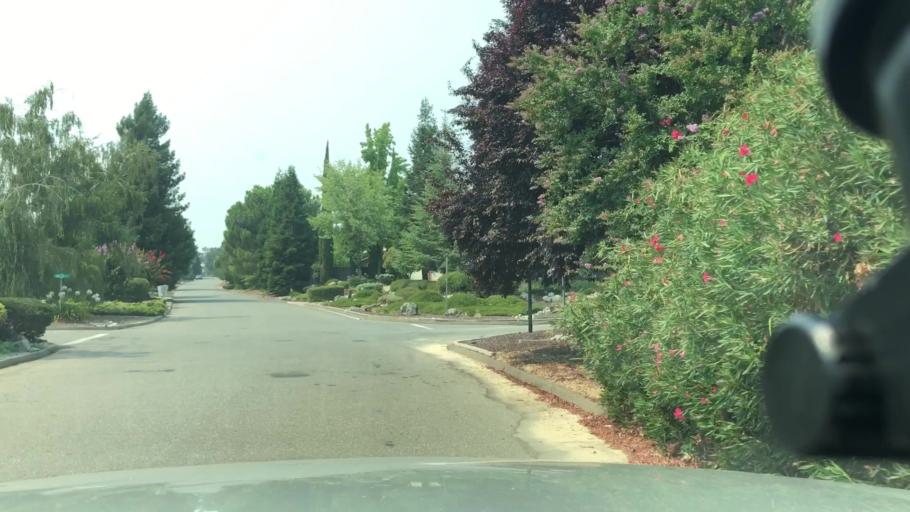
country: US
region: California
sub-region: El Dorado County
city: Cameron Park
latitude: 38.6612
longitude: -121.0054
